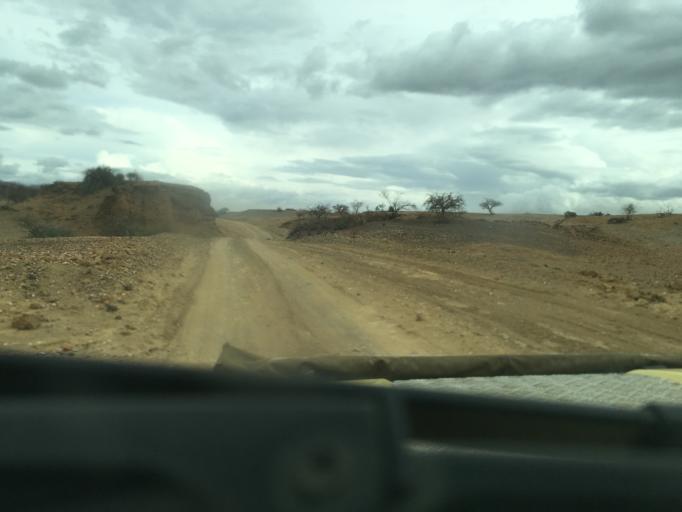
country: KE
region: Kajiado
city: Magadi
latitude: -2.4971
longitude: 35.8714
